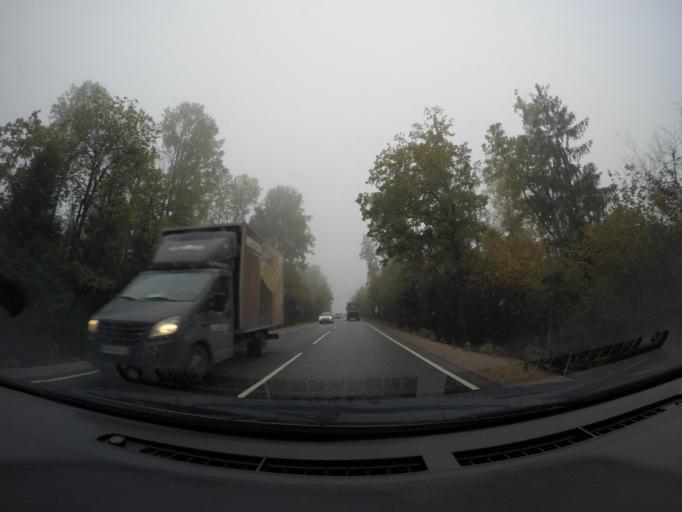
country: RU
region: Moskovskaya
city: Rumyantsevo
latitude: 55.8405
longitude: 36.4634
